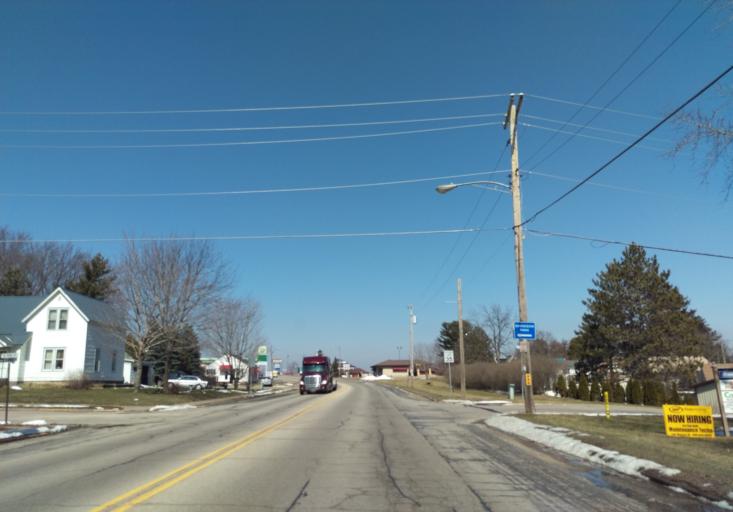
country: US
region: Wisconsin
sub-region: Vernon County
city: Westby
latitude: 43.6564
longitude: -90.8558
